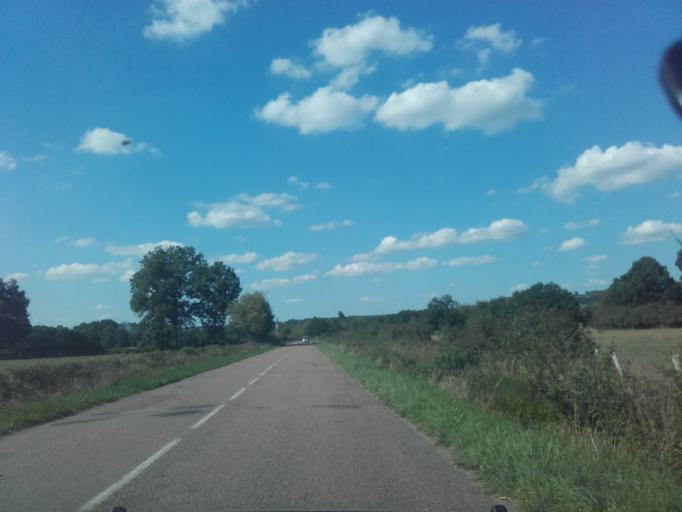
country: FR
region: Bourgogne
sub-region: Departement de Saone-et-Loire
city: Epinac
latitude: 47.0009
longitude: 4.4776
